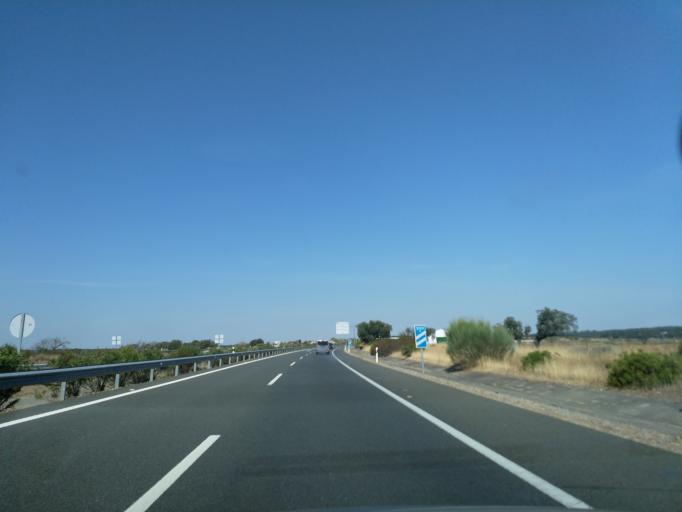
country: ES
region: Extremadura
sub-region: Provincia de Caceres
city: Casas de Don Antonio
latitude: 39.2237
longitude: -6.2984
